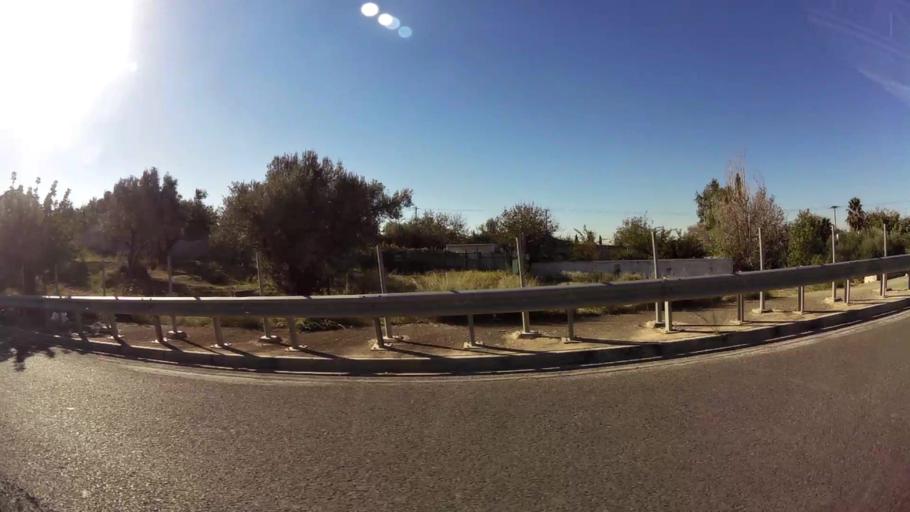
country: GR
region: Attica
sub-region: Nomarchia Athinas
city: Lykovrysi
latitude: 38.0964
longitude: 23.7736
